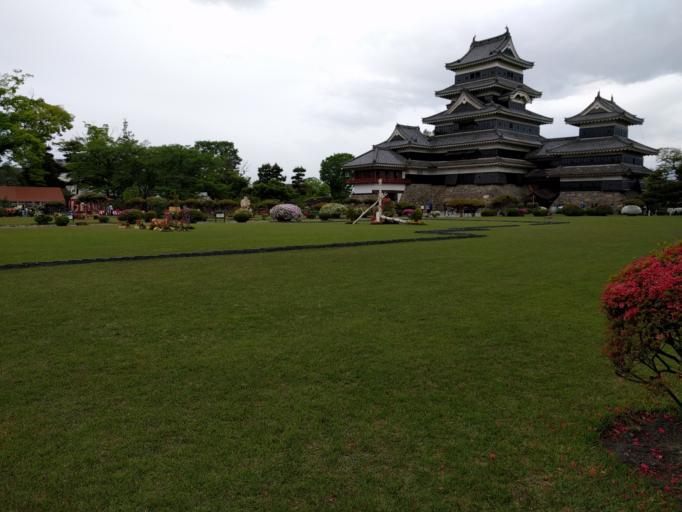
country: JP
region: Nagano
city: Matsumoto
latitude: 36.2391
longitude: 137.9698
